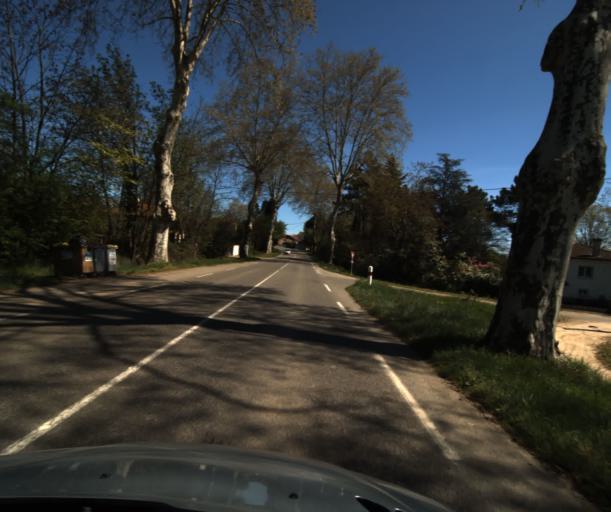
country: FR
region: Midi-Pyrenees
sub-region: Departement du Tarn-et-Garonne
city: Moissac
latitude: 44.1221
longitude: 1.1456
